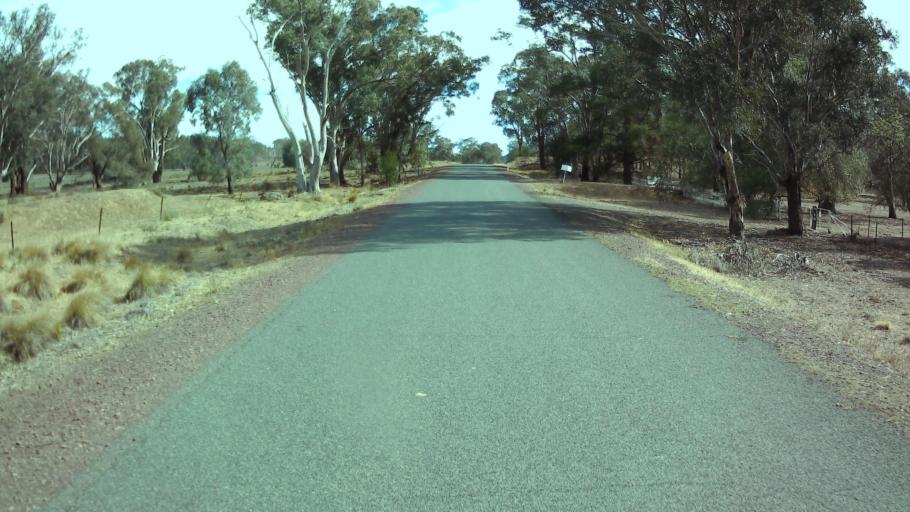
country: AU
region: New South Wales
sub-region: Weddin
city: Grenfell
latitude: -33.8154
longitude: 148.2918
